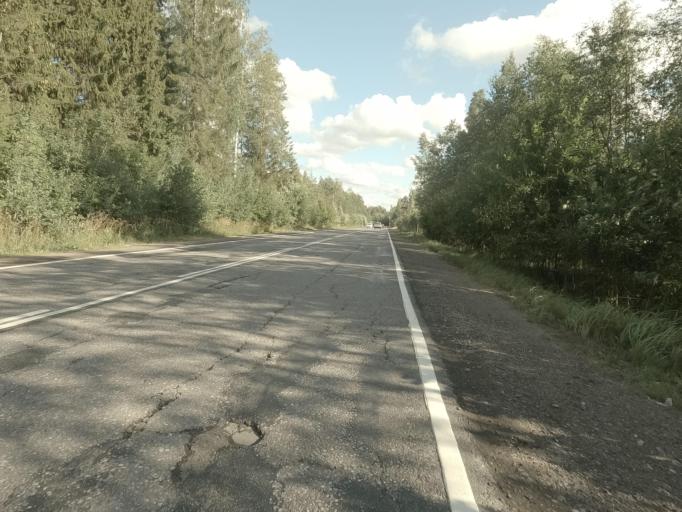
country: RU
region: Leningrad
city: Borisova Griva
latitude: 59.9891
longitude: 30.8857
